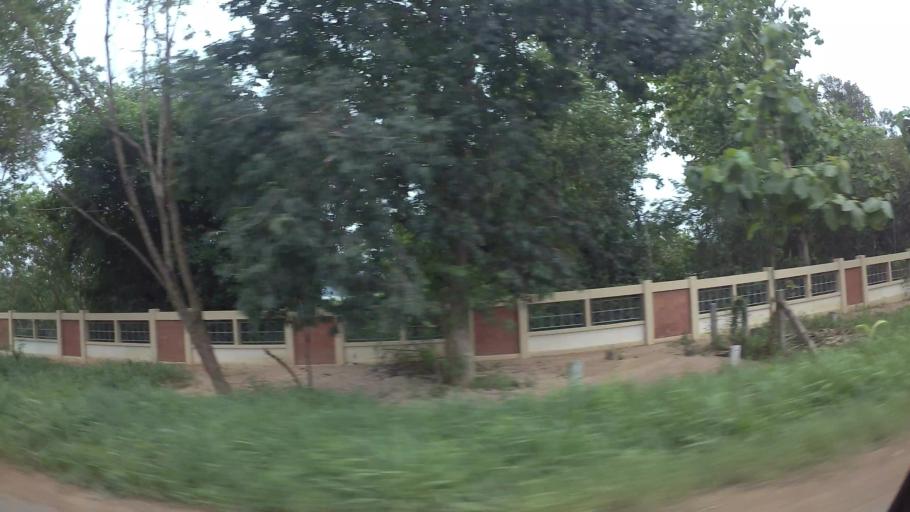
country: TH
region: Chon Buri
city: Si Racha
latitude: 13.1935
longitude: 100.9620
